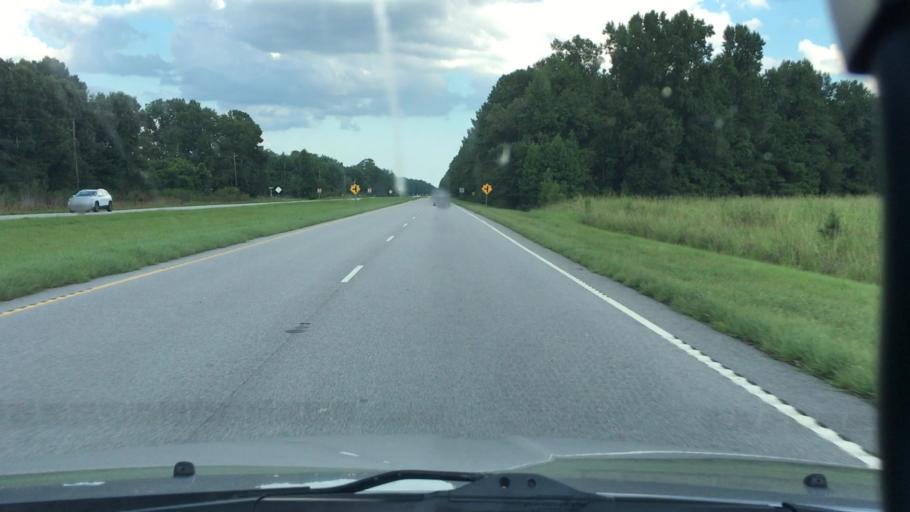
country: US
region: South Carolina
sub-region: Hampton County
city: Yemassee
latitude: 32.6357
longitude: -80.8427
